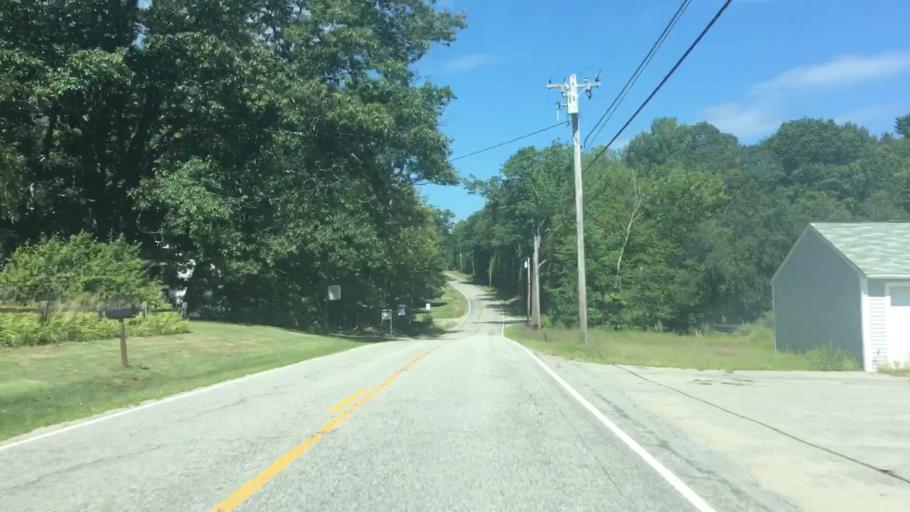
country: US
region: Maine
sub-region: Kennebec County
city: Monmouth
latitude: 44.1633
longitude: -69.9434
